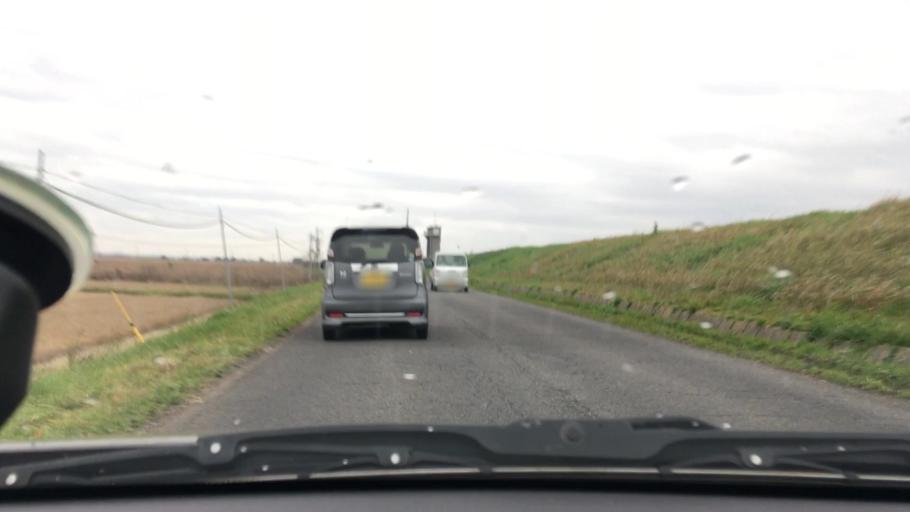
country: JP
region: Chiba
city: Omigawa
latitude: 35.8677
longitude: 140.6220
